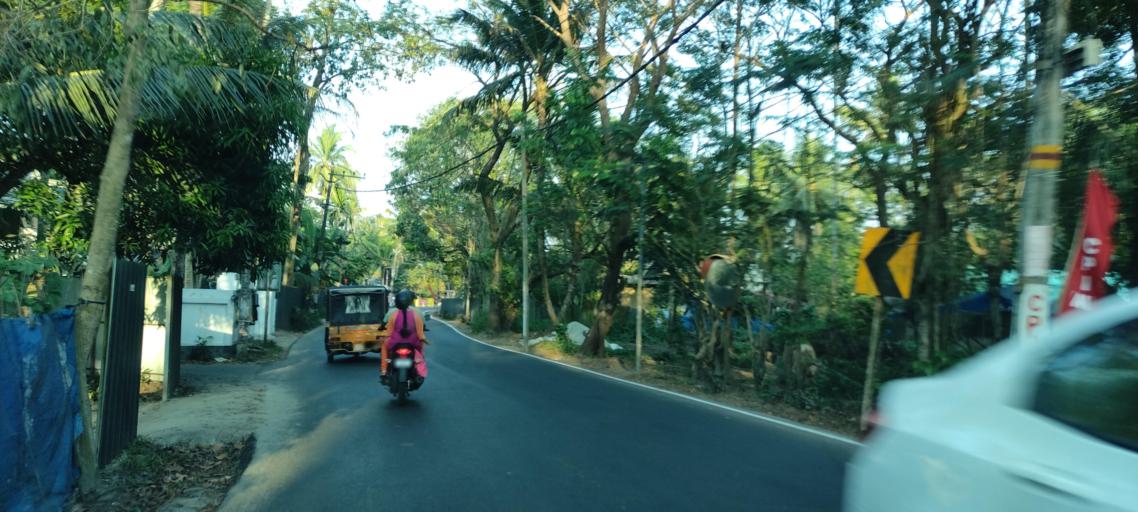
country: IN
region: Kerala
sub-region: Alappuzha
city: Shertallai
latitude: 9.7026
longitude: 76.3546
